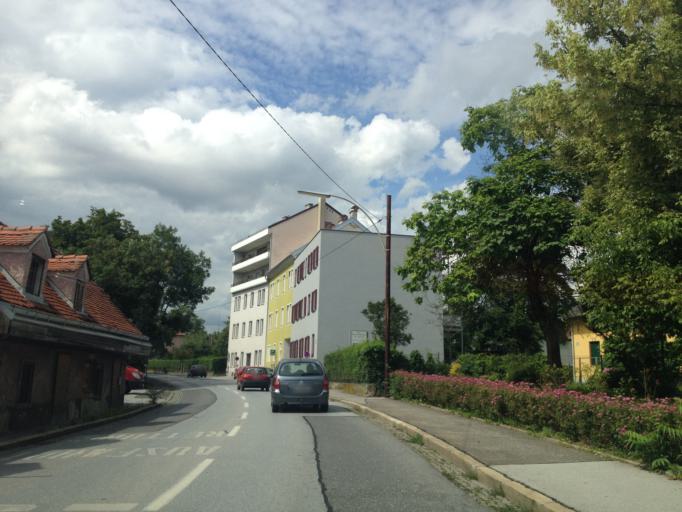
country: AT
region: Styria
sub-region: Graz Stadt
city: Graz
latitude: 47.0547
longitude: 15.4548
